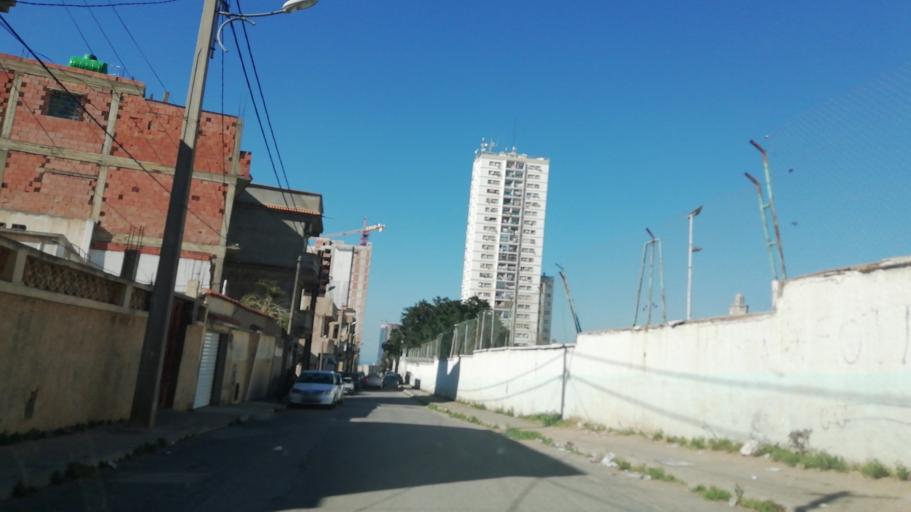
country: DZ
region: Oran
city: Oran
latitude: 35.7044
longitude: -0.6161
